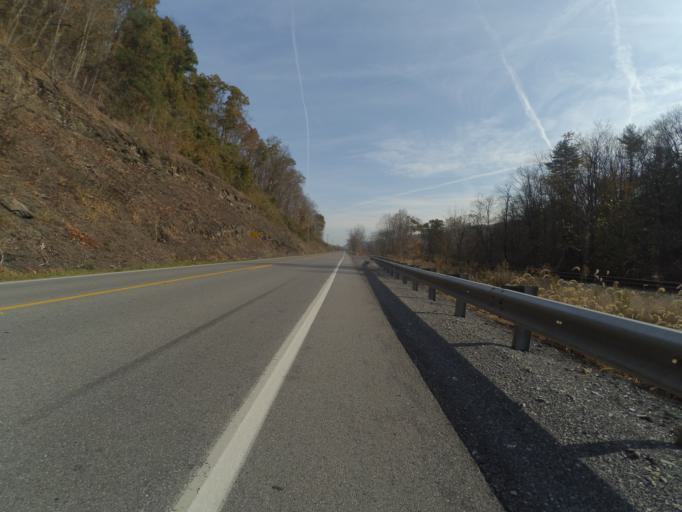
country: US
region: Pennsylvania
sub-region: Centre County
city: Park Forest Village
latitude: 40.8526
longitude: -77.9651
